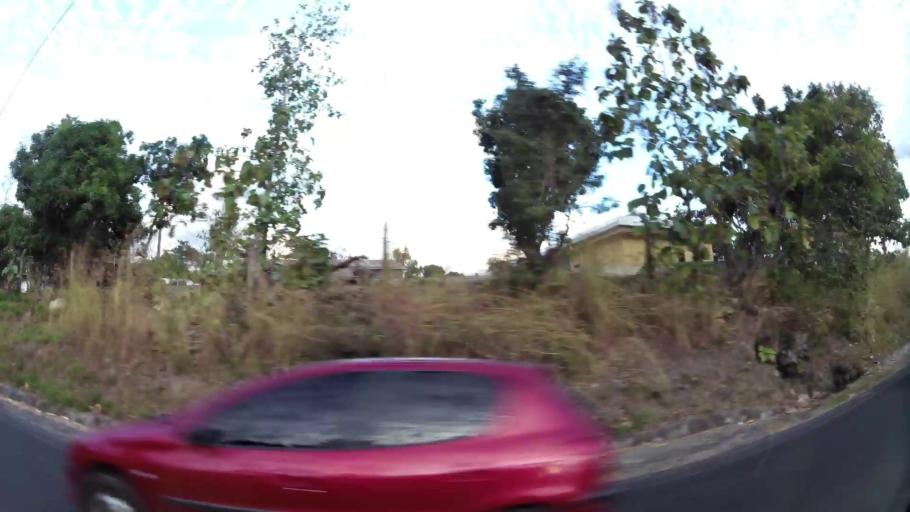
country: SV
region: San Vicente
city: Apastepeque
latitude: 13.6646
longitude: -88.7947
